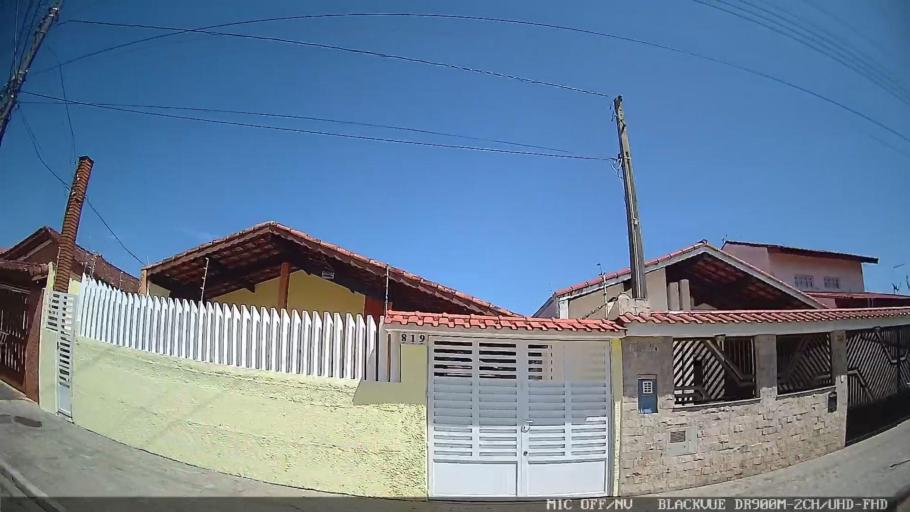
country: BR
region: Sao Paulo
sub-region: Peruibe
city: Peruibe
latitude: -24.2991
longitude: -46.9777
